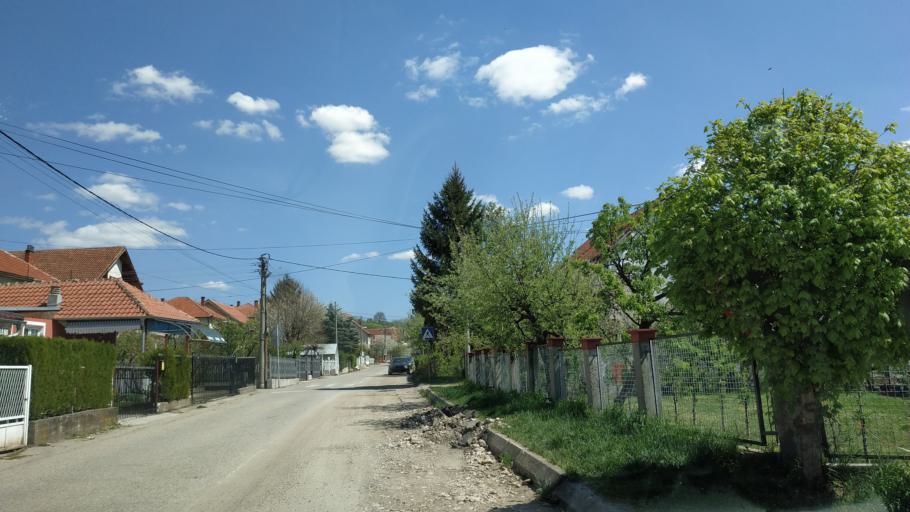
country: RS
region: Central Serbia
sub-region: Zajecarski Okrug
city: Soko Banja
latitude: 43.6491
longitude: 21.8783
